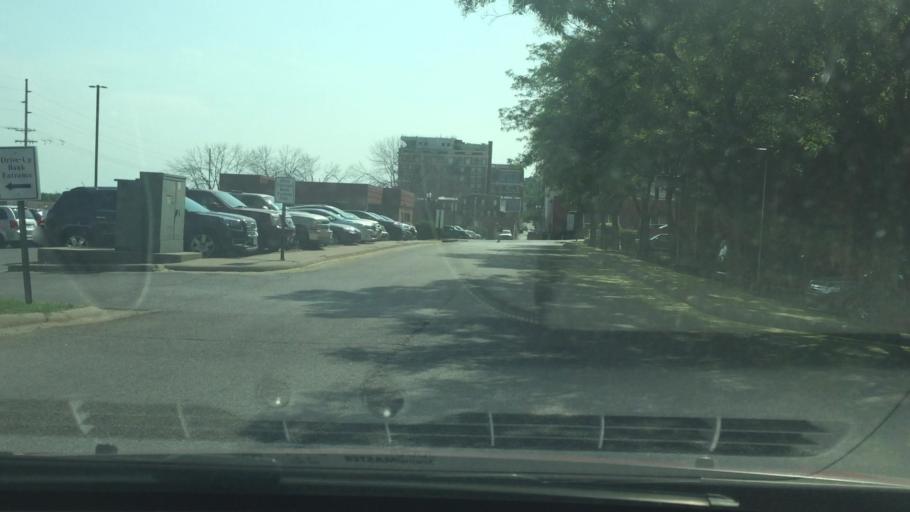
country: US
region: Iowa
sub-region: Muscatine County
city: Muscatine
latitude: 41.4226
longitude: -91.0423
